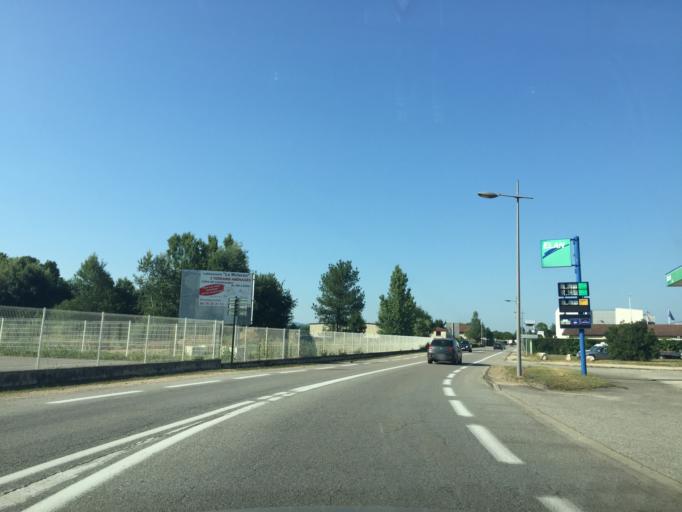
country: FR
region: Rhone-Alpes
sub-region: Departement de l'Isere
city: Saint-Romans
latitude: 45.1110
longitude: 5.3201
